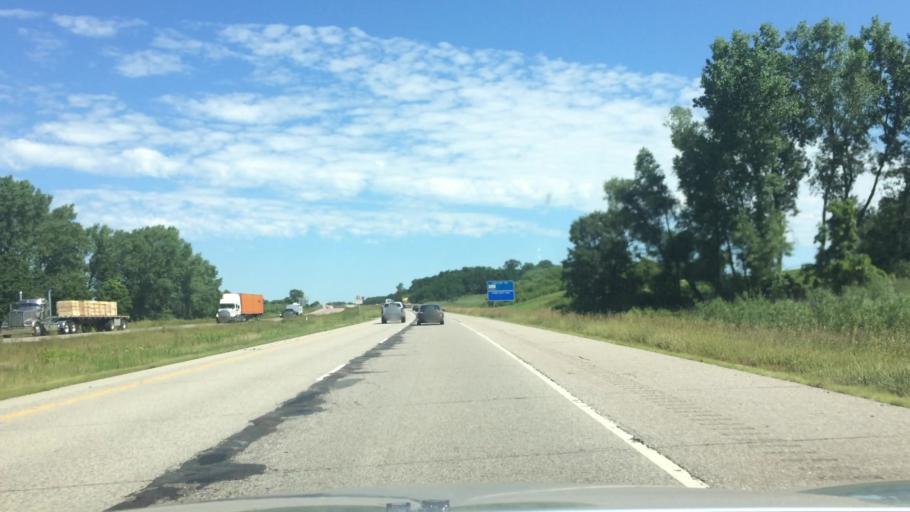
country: US
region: Wisconsin
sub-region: Columbia County
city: Portage
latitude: 43.6908
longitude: -89.4696
